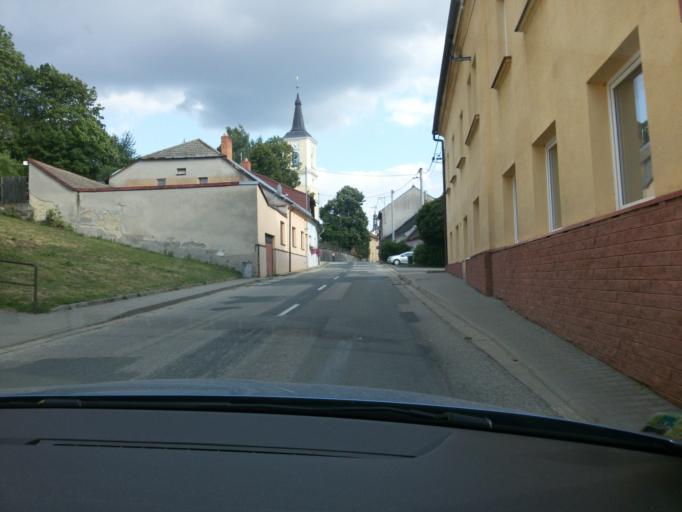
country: CZ
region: South Moravian
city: Olesnice
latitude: 49.5598
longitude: 16.4193
